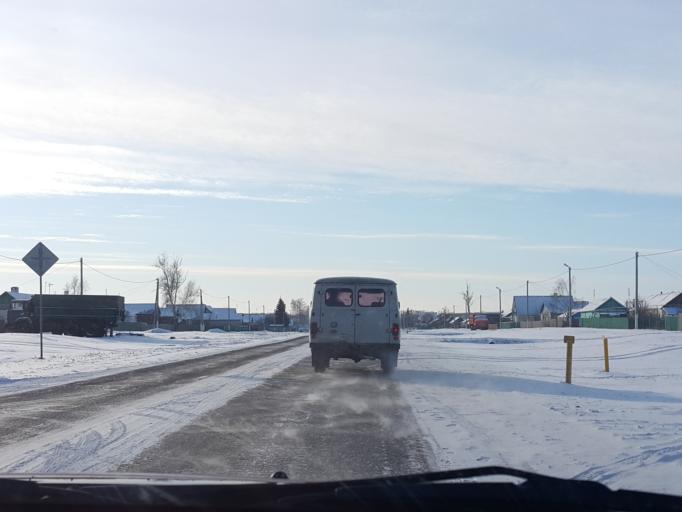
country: RU
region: Tambov
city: Znamenka
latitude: 52.4158
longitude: 41.4272
